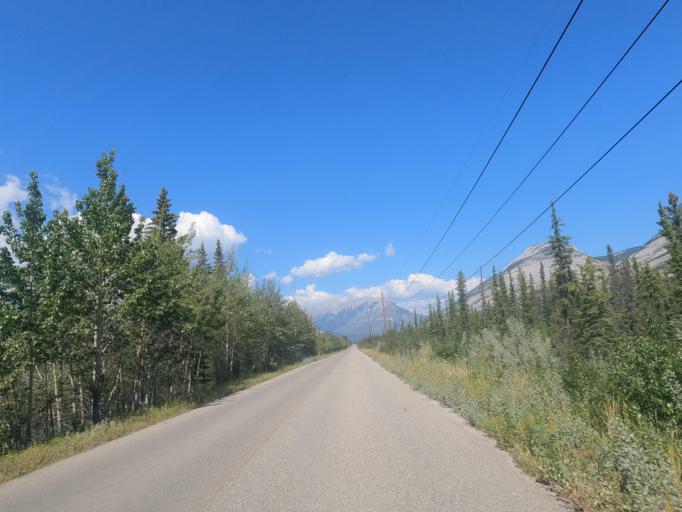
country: CA
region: Alberta
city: Jasper Park Lodge
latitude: 53.0009
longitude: -118.0849
